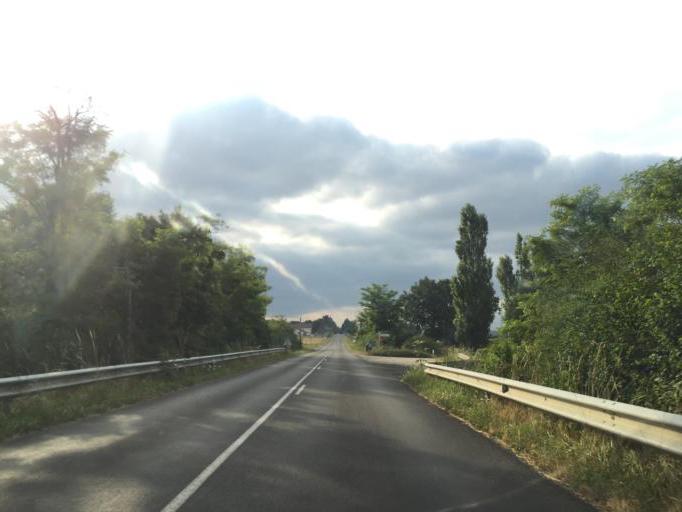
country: FR
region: Auvergne
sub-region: Departement de l'Allier
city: Yzeure
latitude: 46.5477
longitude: 3.3738
